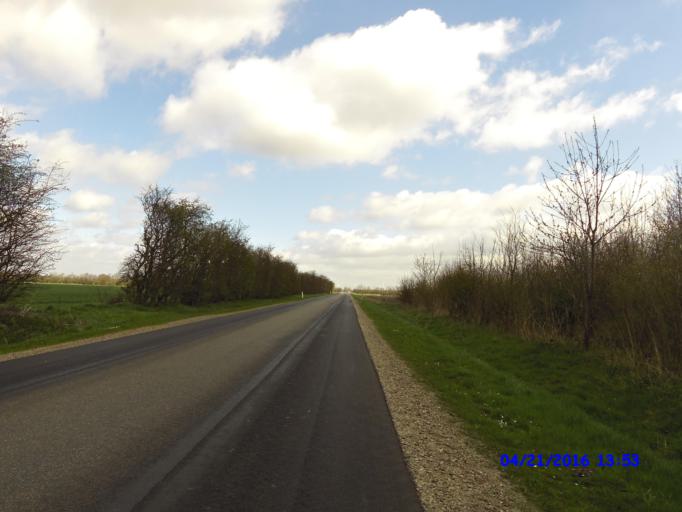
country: DK
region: South Denmark
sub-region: Haderslev Kommune
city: Gram
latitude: 55.2449
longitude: 9.0194
